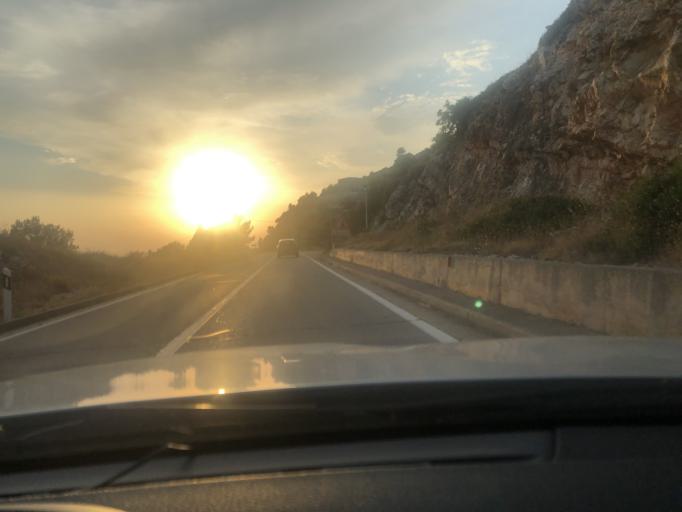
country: HR
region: Splitsko-Dalmatinska
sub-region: Grad Hvar
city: Hvar
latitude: 43.1519
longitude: 16.5165
